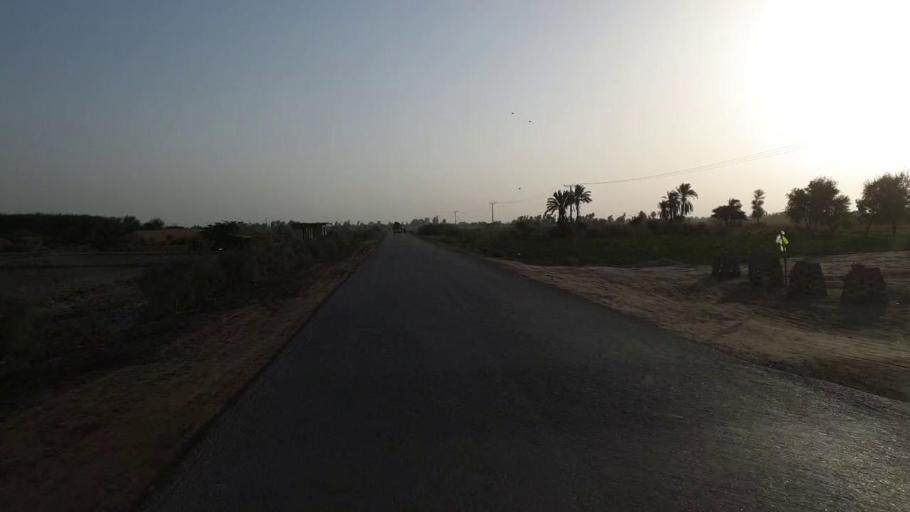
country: PK
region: Sindh
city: Jam Sahib
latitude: 26.2793
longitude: 68.5721
